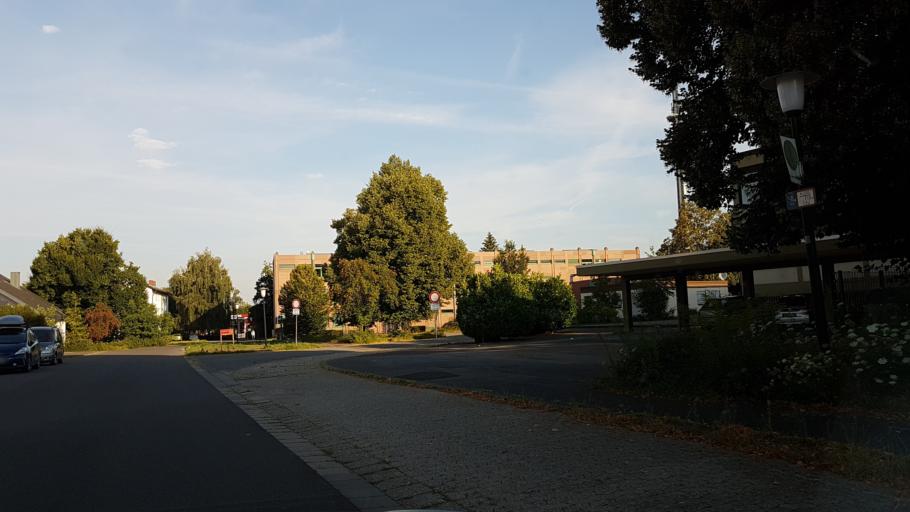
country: DE
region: Saarland
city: Homburg
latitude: 49.3147
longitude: 7.3388
